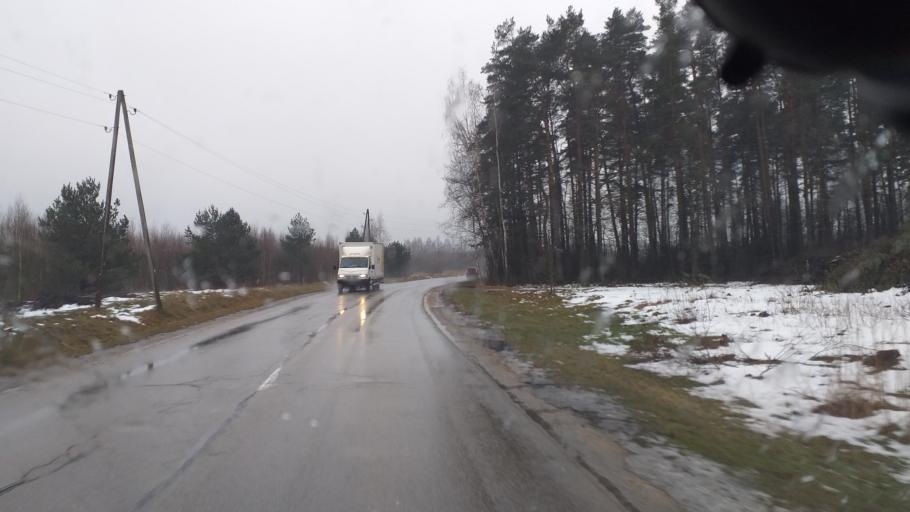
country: LV
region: Babite
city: Pinki
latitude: 56.9718
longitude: 23.9695
